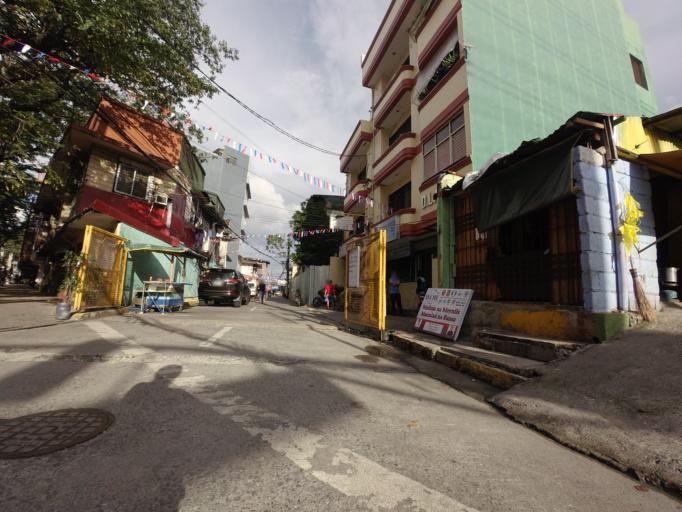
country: PH
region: Metro Manila
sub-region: City of Manila
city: Quiapo
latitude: 14.5888
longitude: 120.9848
